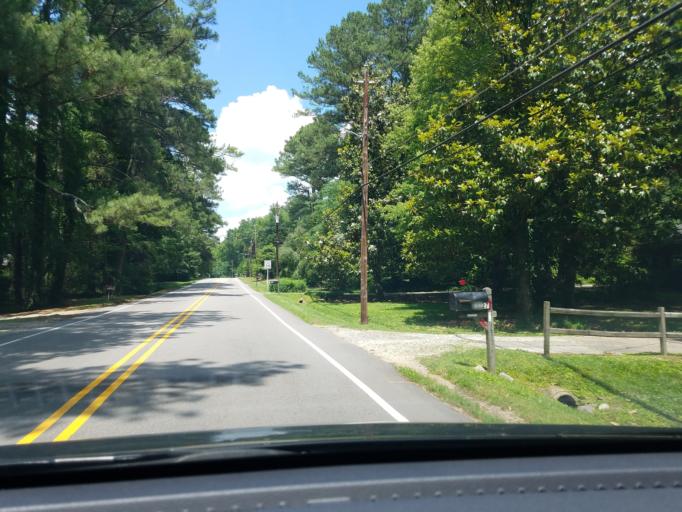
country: US
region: North Carolina
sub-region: Durham County
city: Durham
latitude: 35.9475
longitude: -78.9410
